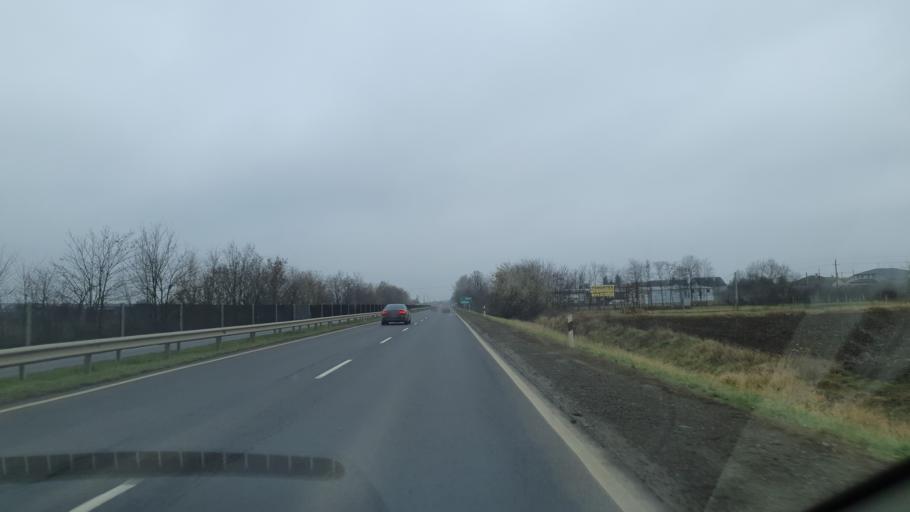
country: HU
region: Szabolcs-Szatmar-Bereg
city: Nyiregyhaza
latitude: 47.9078
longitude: 21.7128
